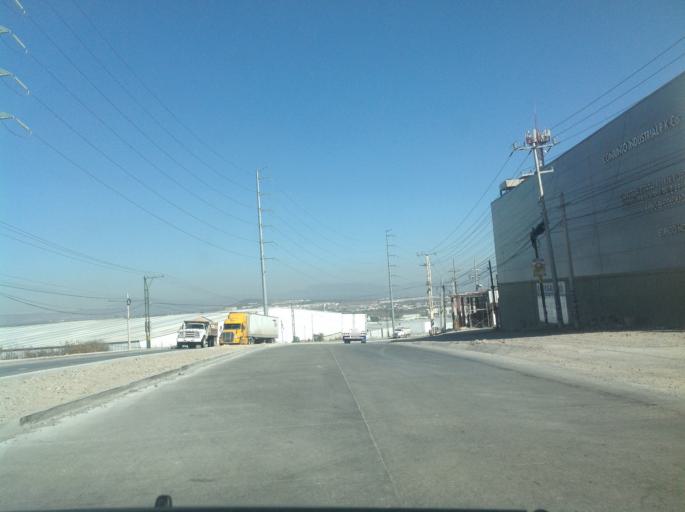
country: MX
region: Queretaro
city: El Colorado
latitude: 20.5640
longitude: -100.2678
